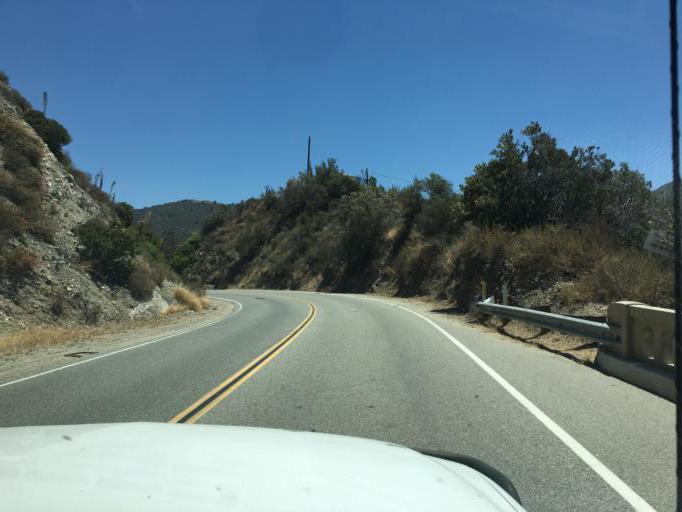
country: US
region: California
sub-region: Los Angeles County
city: Glendora
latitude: 34.1843
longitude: -117.8744
